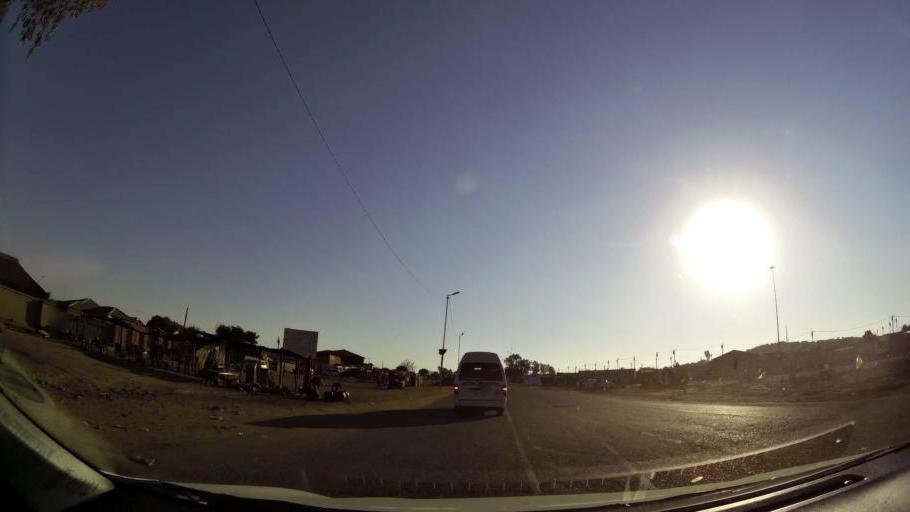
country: ZA
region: Gauteng
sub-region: City of Tshwane Metropolitan Municipality
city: Cullinan
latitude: -25.6981
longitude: 28.4188
